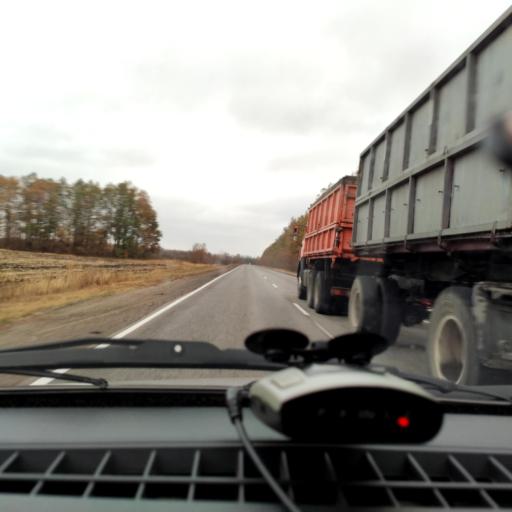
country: RU
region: Voronezj
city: Shilovo
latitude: 51.3979
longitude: 39.0028
